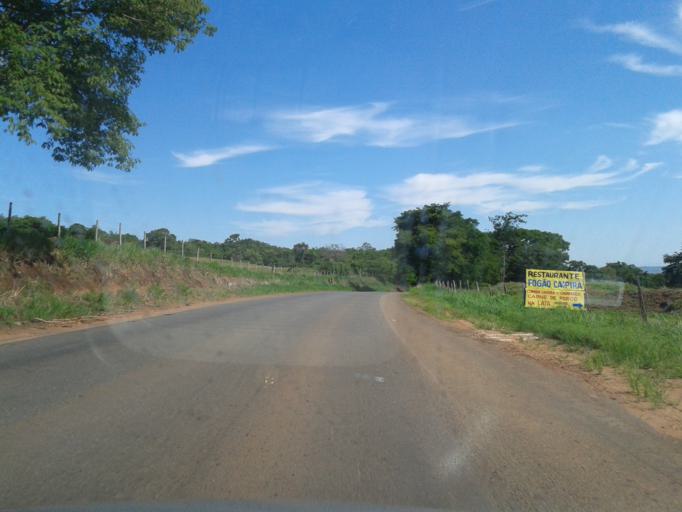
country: BR
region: Goias
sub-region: Piracanjuba
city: Piracanjuba
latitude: -17.2273
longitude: -48.7136
